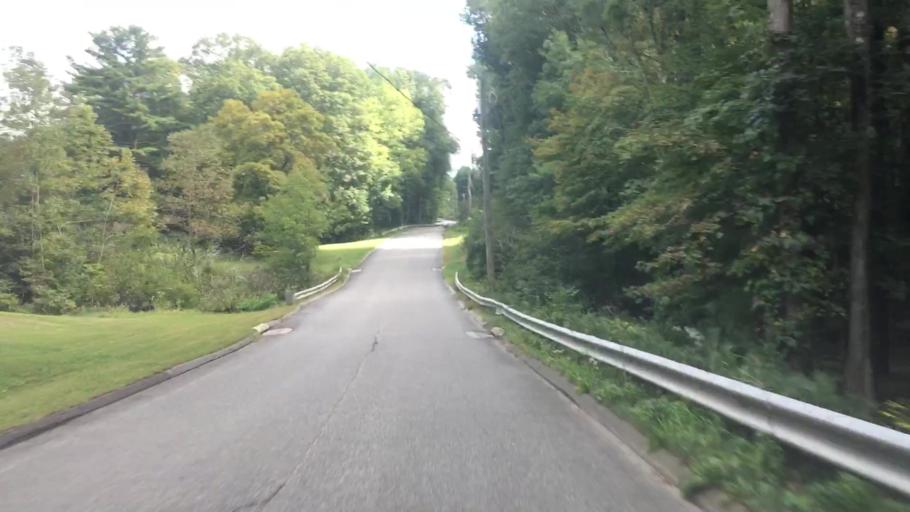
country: US
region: Connecticut
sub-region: Tolland County
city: Stafford Springs
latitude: 41.9173
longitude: -72.2225
